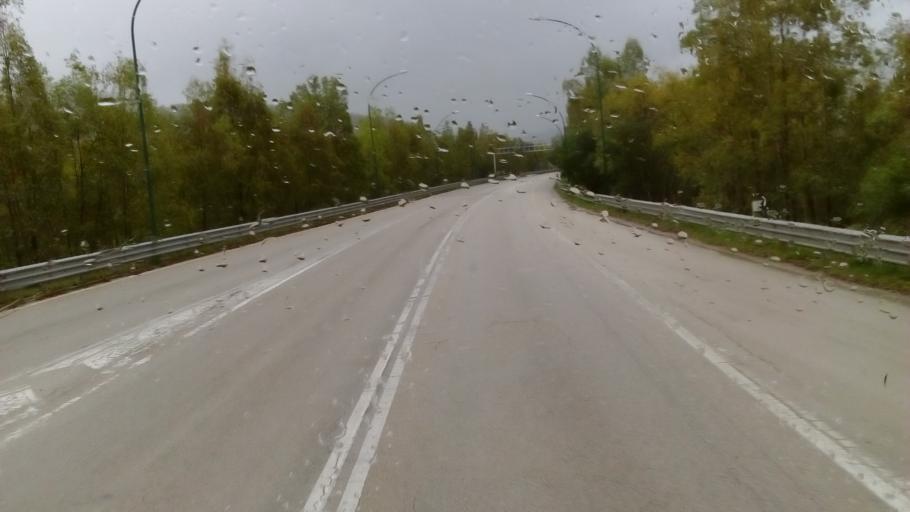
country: IT
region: Sicily
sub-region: Enna
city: Villarosa
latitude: 37.5354
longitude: 14.1295
